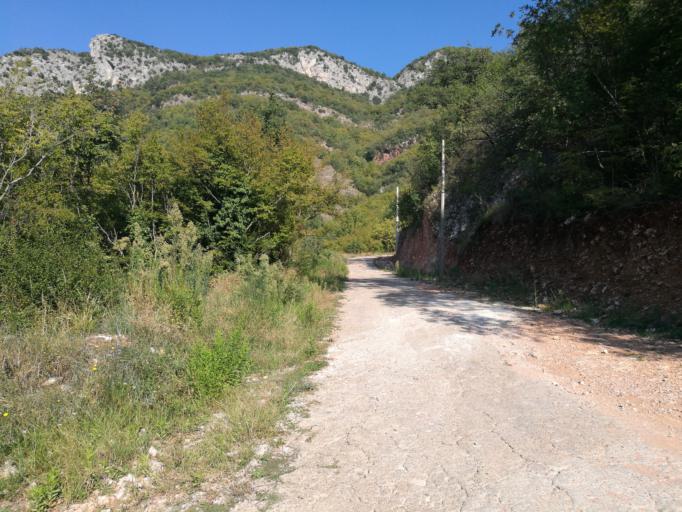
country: ME
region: Budva
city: Budva
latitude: 42.2864
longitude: 18.8867
